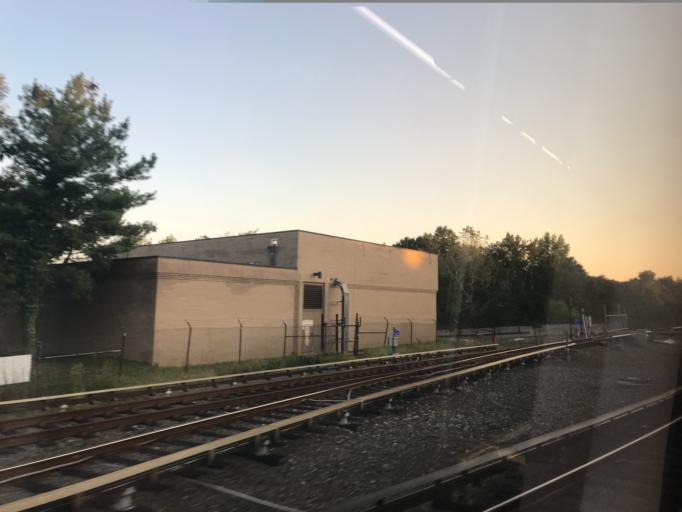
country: US
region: Maryland
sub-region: Prince George's County
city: Berwyn Heights
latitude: 39.0099
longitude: -76.9122
